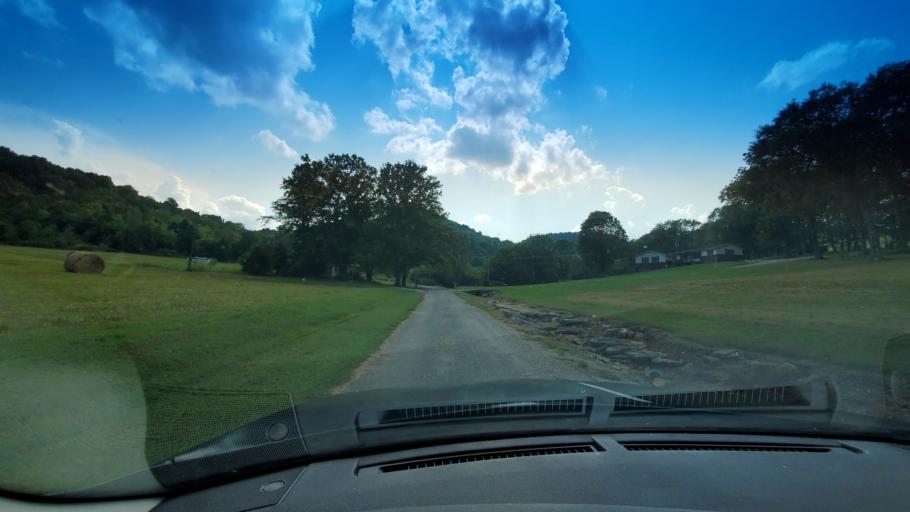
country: US
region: Tennessee
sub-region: Smith County
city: South Carthage
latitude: 36.2241
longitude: -85.9835
